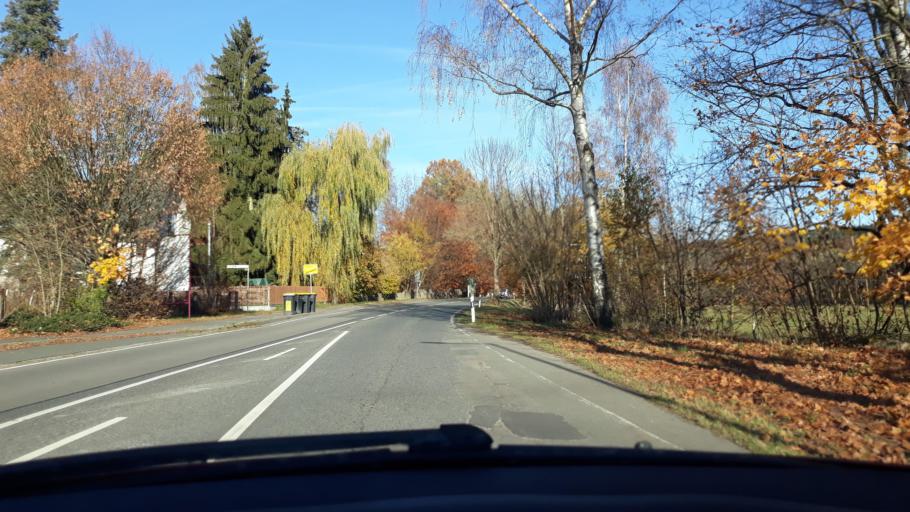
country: DE
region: Saxony
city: Kirchberg
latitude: 50.6304
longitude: 12.5192
